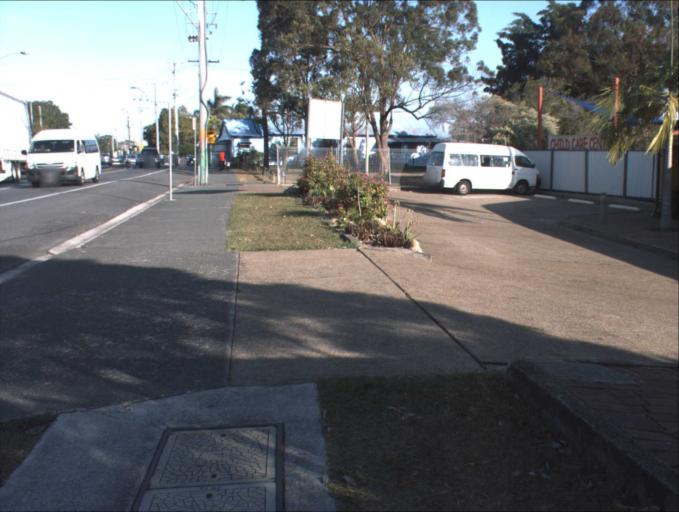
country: AU
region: Queensland
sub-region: Logan
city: Woodridge
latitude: -27.6375
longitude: 153.1015
